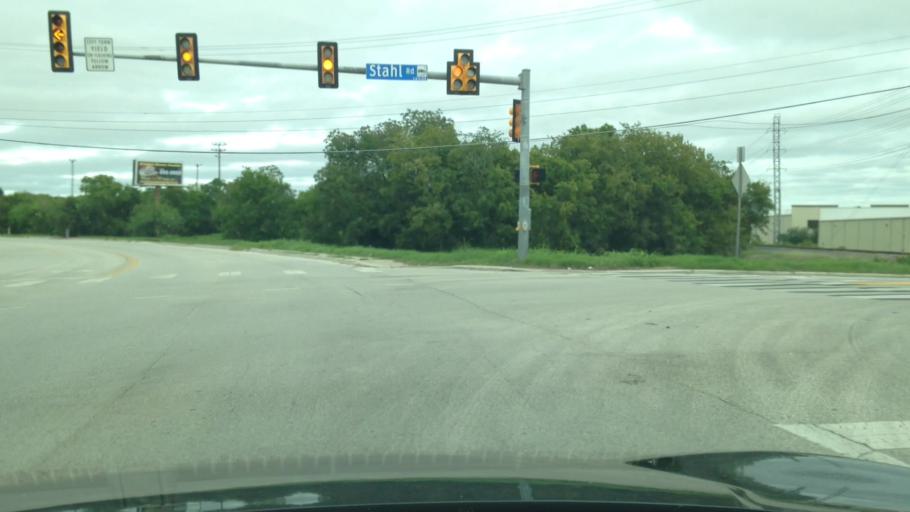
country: US
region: Texas
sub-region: Bexar County
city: Windcrest
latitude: 29.5646
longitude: -98.4191
